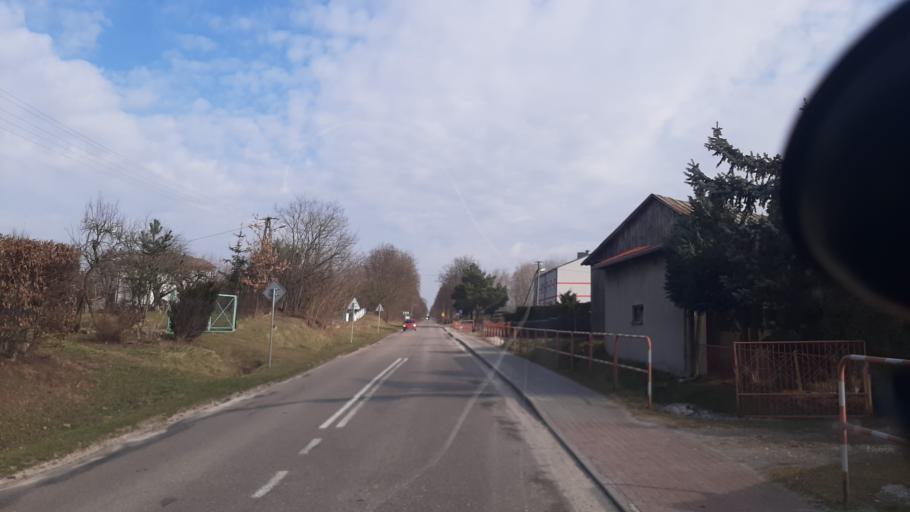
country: PL
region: Lublin Voivodeship
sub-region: Powiat lubartowski
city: Wola Sernicka
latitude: 51.4531
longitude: 22.6742
